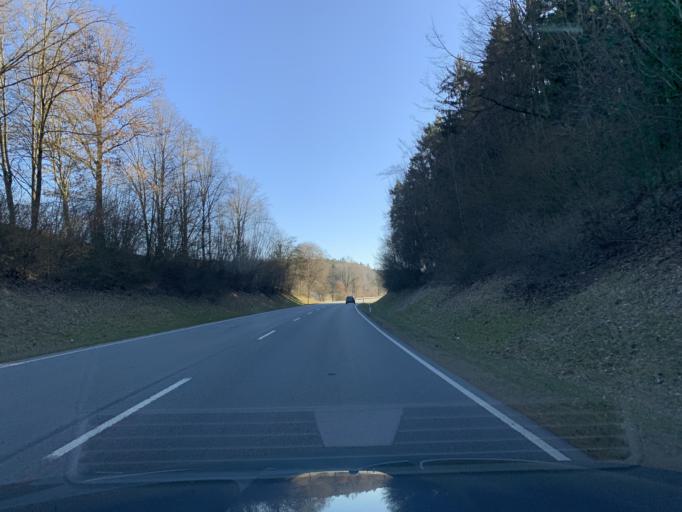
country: DE
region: Bavaria
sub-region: Upper Palatinate
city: Schonthal
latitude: 49.3254
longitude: 12.6330
